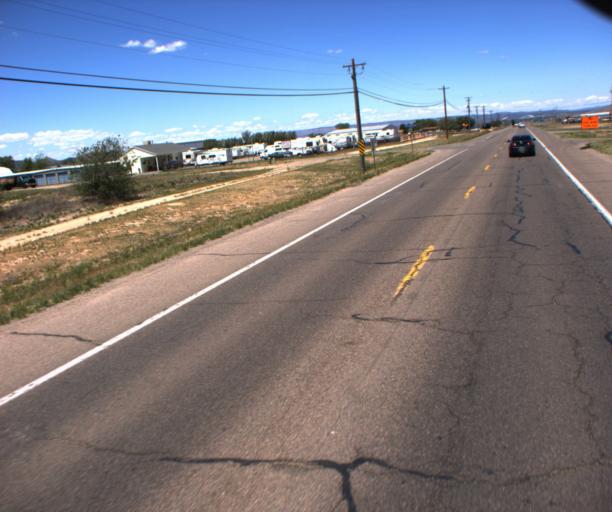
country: US
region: Arizona
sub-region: Yavapai County
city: Chino Valley
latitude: 34.7825
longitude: -112.4524
